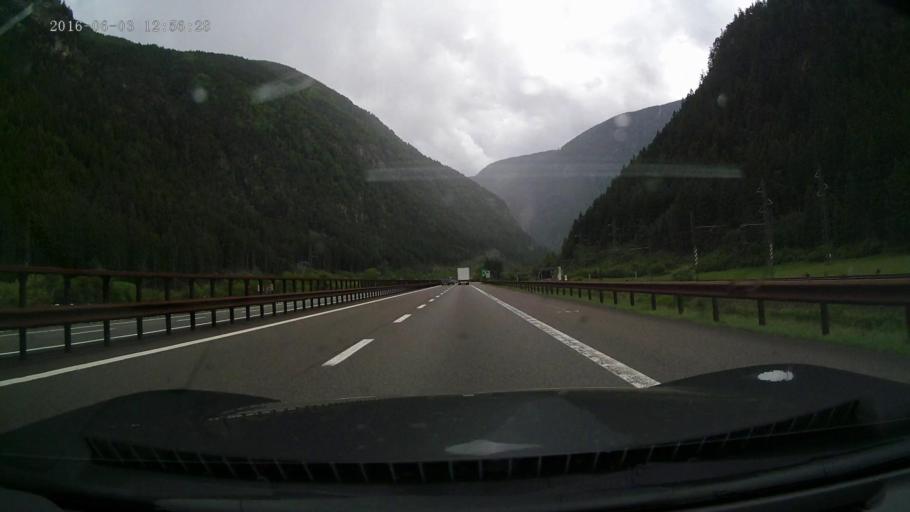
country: IT
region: Trentino-Alto Adige
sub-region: Bolzano
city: Campo di Trens
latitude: 46.8324
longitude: 11.5330
